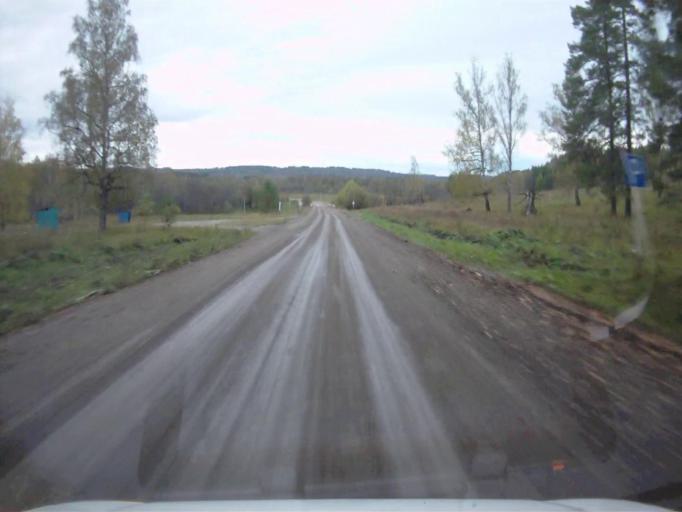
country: RU
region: Chelyabinsk
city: Nyazepetrovsk
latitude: 56.1232
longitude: 59.3581
